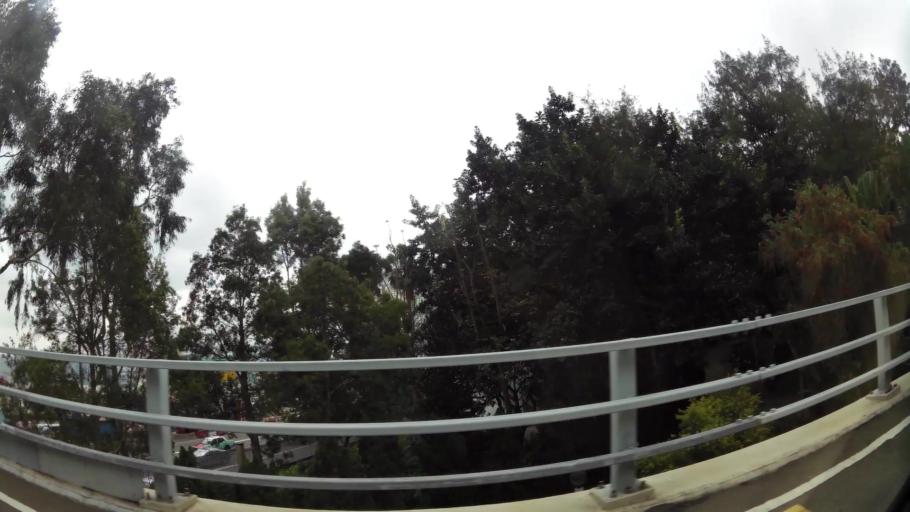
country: HK
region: Wanchai
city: Wan Chai
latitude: 22.2835
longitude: 114.1861
